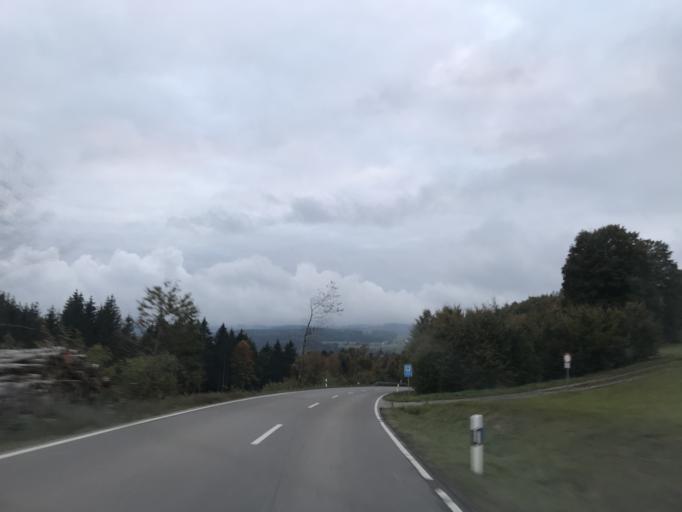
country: DE
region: Baden-Wuerttemberg
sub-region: Freiburg Region
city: Rickenbach
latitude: 47.6212
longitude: 8.0318
